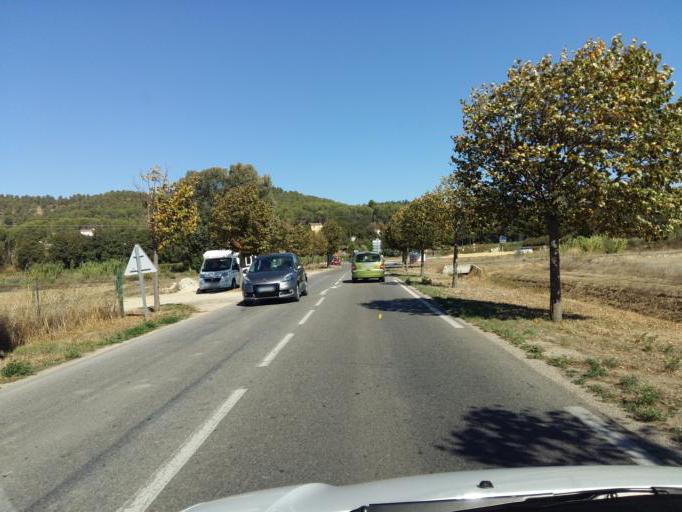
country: FR
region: Provence-Alpes-Cote d'Azur
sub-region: Departement du Vaucluse
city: Villelaure
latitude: 43.7039
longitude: 5.4452
